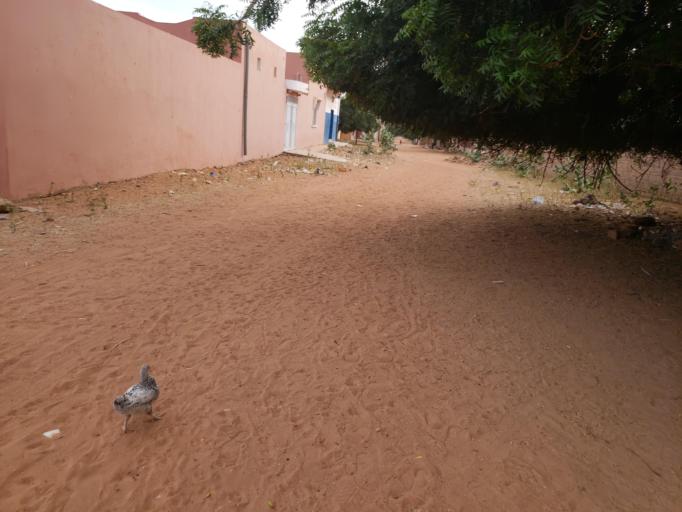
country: SN
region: Louga
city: Ndibene Dahra
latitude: 15.3980
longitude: -15.1120
